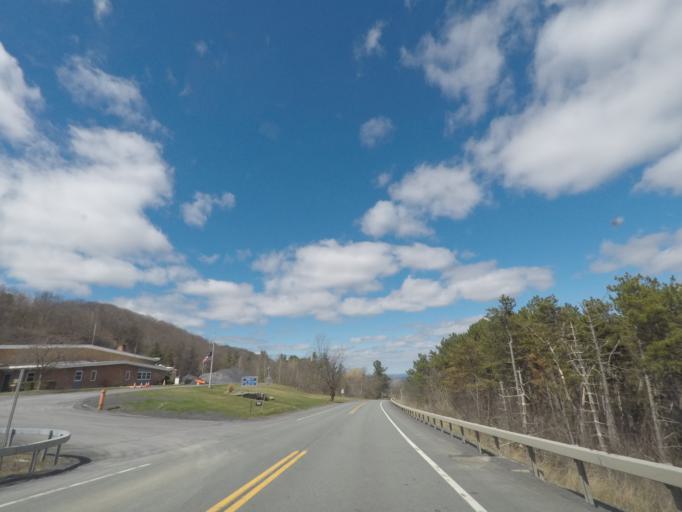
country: US
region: New York
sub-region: Albany County
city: Voorheesville
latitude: 42.6169
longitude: -73.9755
